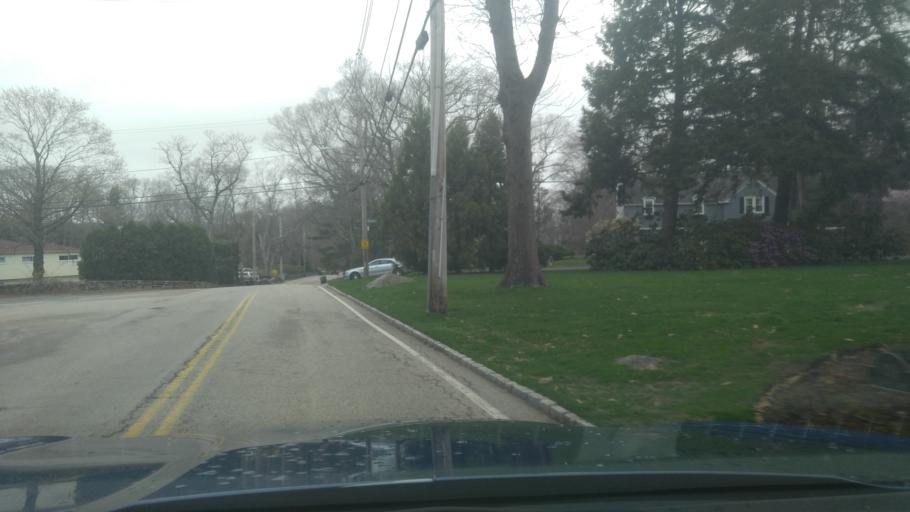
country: US
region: Rhode Island
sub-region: Kent County
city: East Greenwich
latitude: 41.6818
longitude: -71.4612
